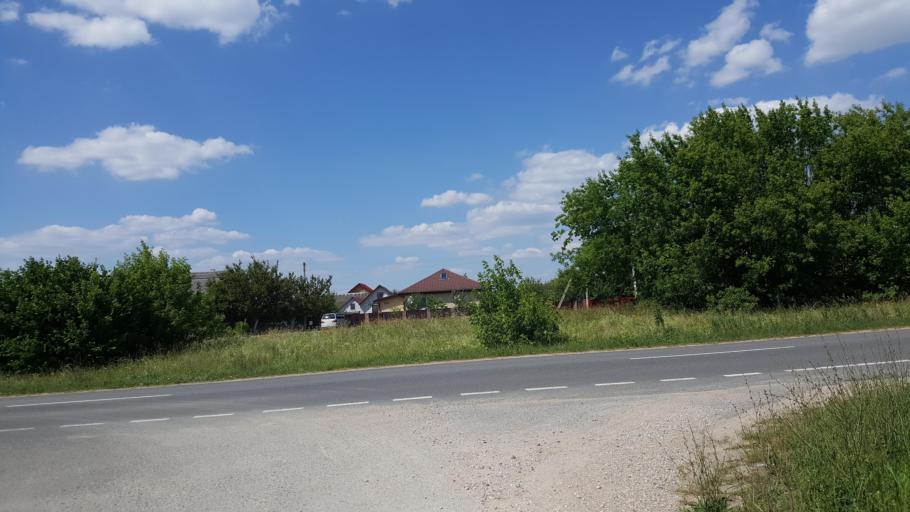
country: BY
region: Brest
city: Kamyanyets
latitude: 52.4025
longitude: 23.8446
